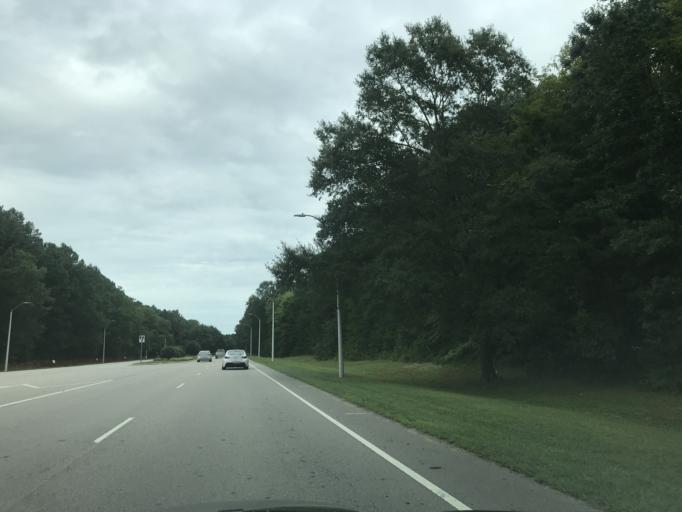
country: US
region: North Carolina
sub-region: Wake County
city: Cary
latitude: 35.7778
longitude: -78.7560
